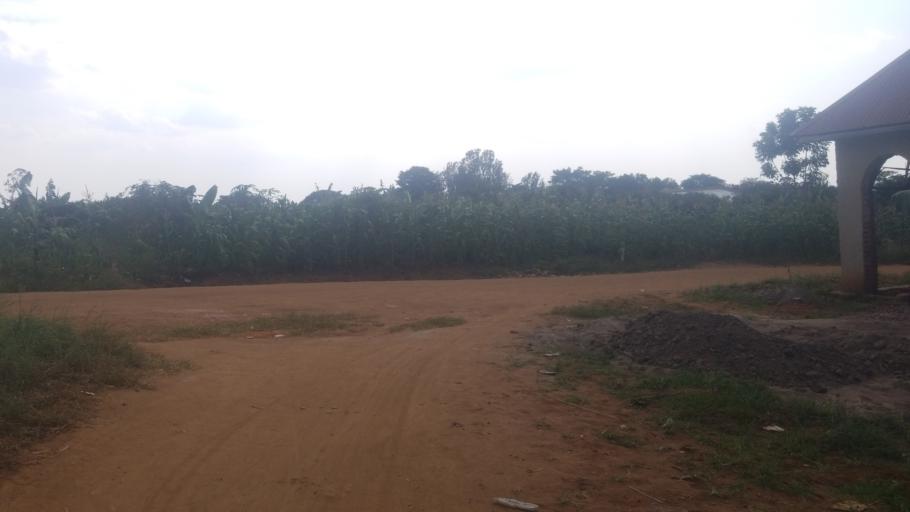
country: UG
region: Central Region
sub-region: Sembabule District
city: Sembabule
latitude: -0.0841
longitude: 31.4580
